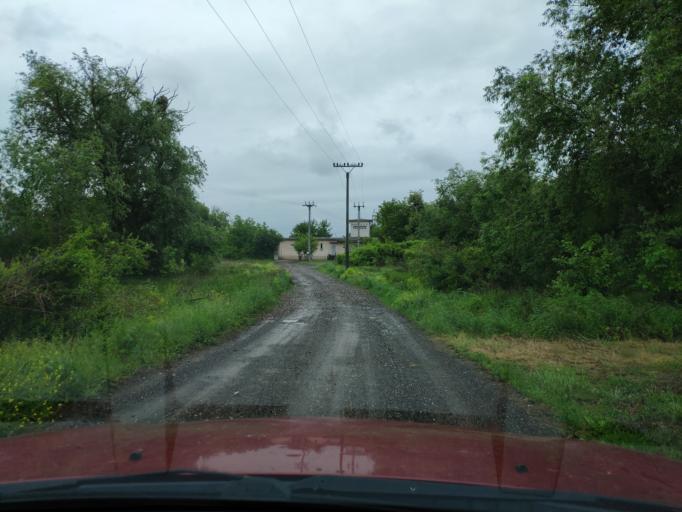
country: SK
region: Kosicky
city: Cierna nad Tisou
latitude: 48.4246
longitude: 22.0826
